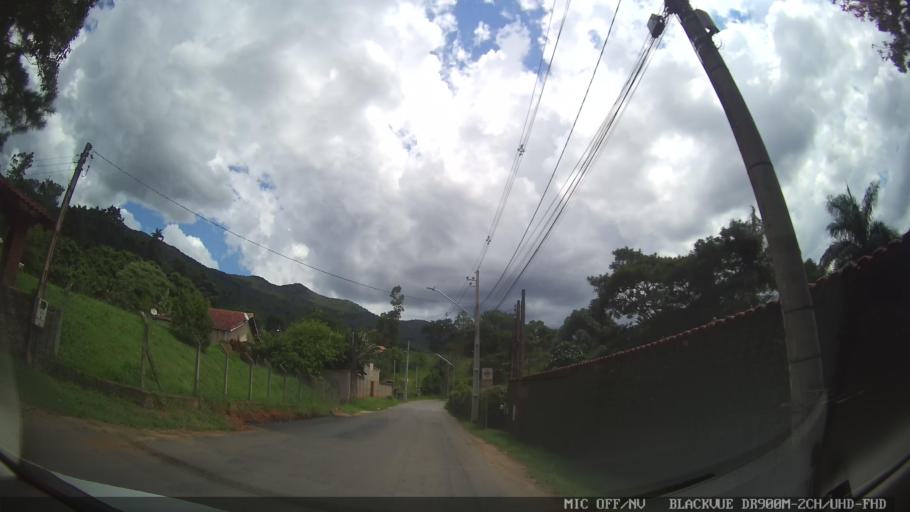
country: BR
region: Minas Gerais
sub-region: Extrema
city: Extrema
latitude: -22.8496
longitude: -46.3004
